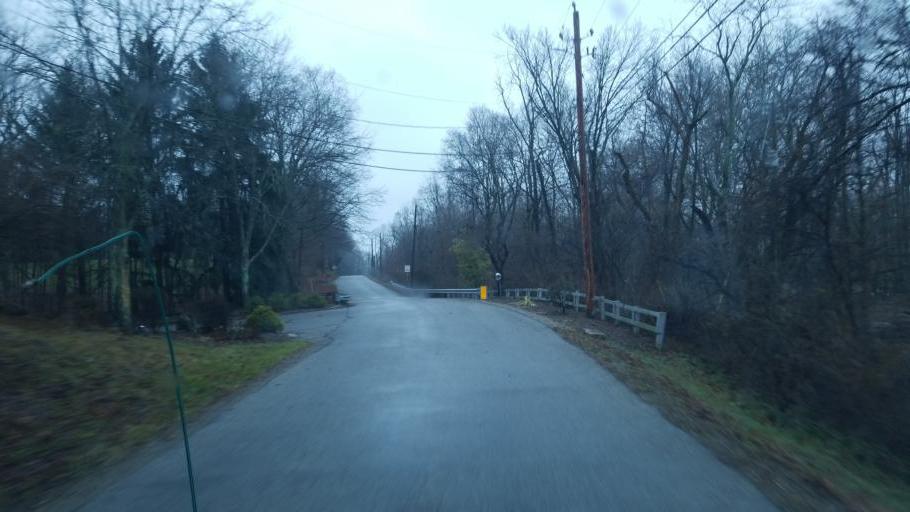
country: US
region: Ohio
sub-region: Delaware County
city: Powell
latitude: 40.1882
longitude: -83.0496
